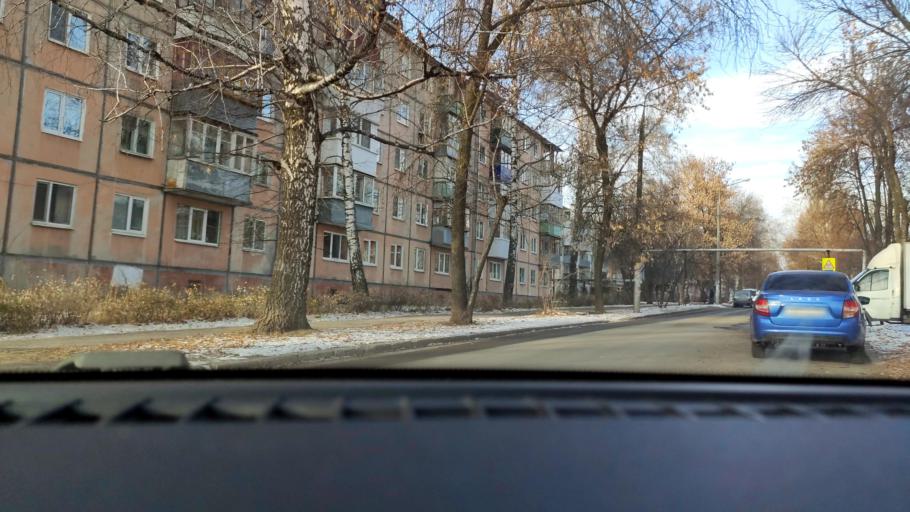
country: RU
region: Samara
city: Petra-Dubrava
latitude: 53.3007
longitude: 50.2724
